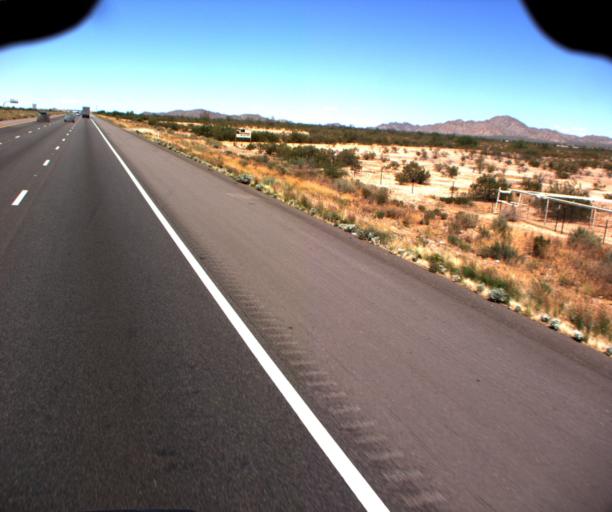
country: US
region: Arizona
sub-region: Pinal County
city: Casa Grande
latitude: 32.9509
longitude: -111.7107
